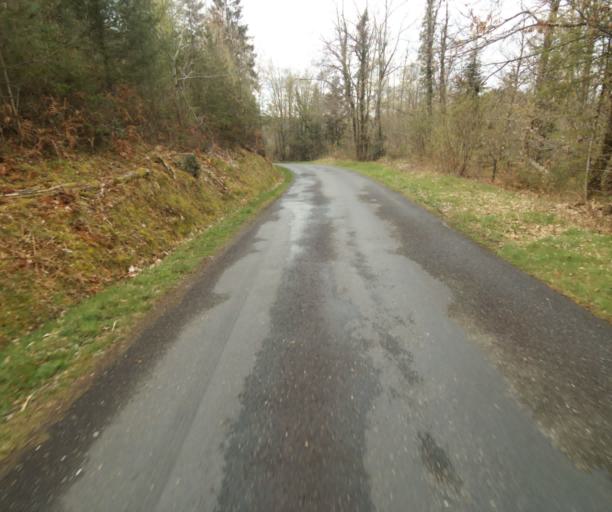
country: FR
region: Limousin
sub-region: Departement de la Correze
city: Tulle
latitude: 45.2802
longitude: 1.7401
